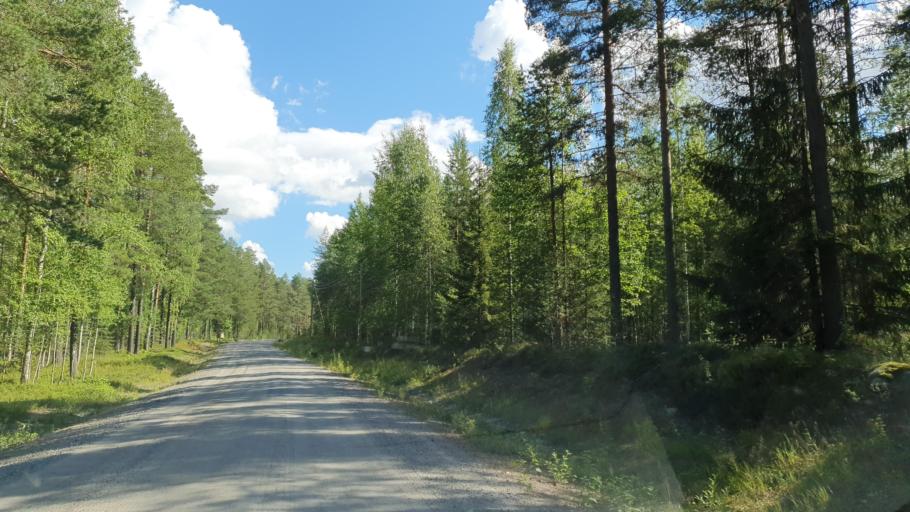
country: FI
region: Kainuu
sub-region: Kehys-Kainuu
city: Kuhmo
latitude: 64.1057
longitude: 29.3960
